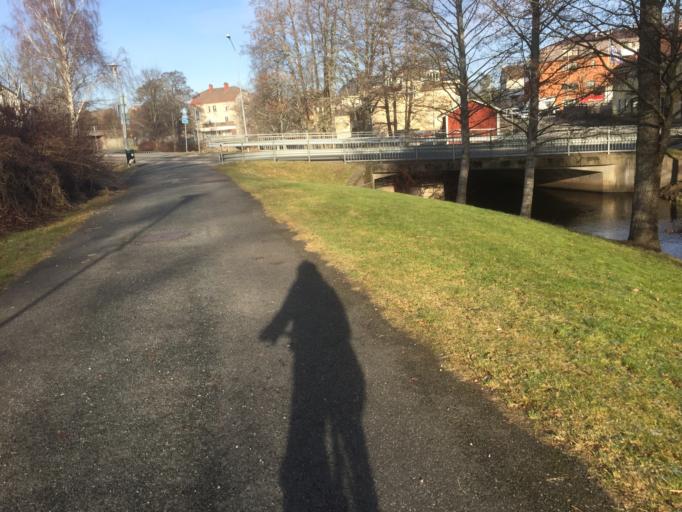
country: SE
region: Joenkoeping
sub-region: Aneby Kommun
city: Aneby
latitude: 57.8376
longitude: 14.8141
